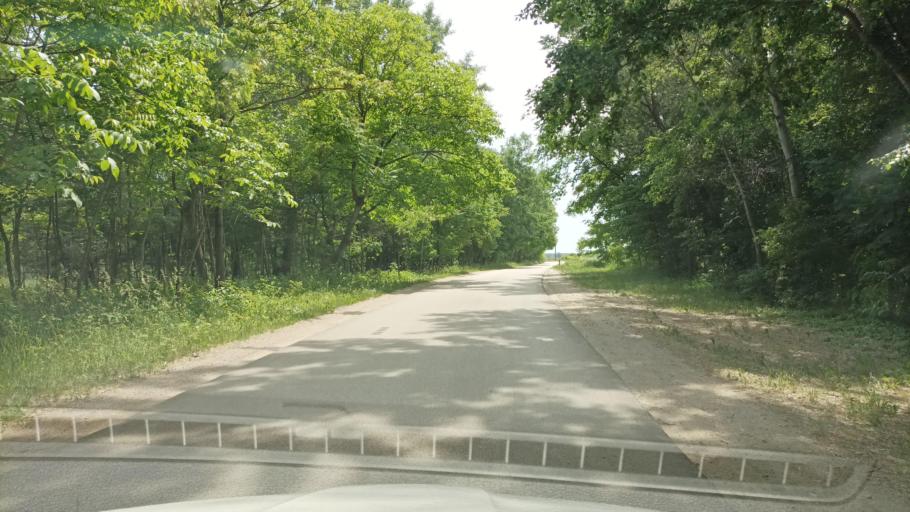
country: HU
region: Pest
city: Rackeve
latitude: 47.1266
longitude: 18.9529
